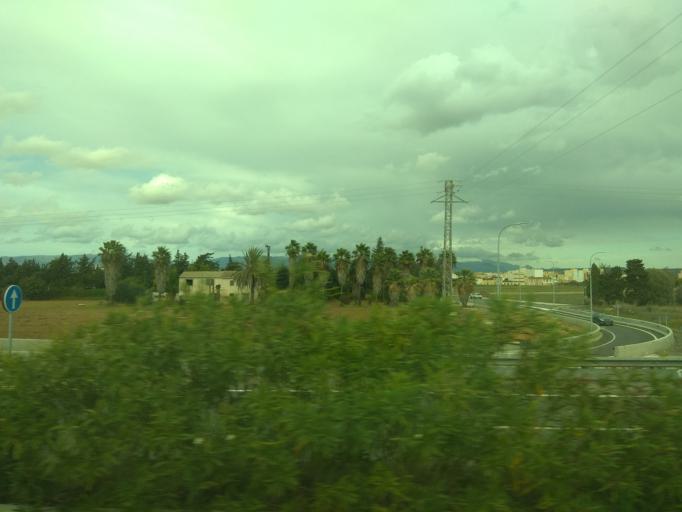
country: ES
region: Balearic Islands
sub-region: Illes Balears
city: Palma
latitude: 39.5676
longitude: 2.7152
